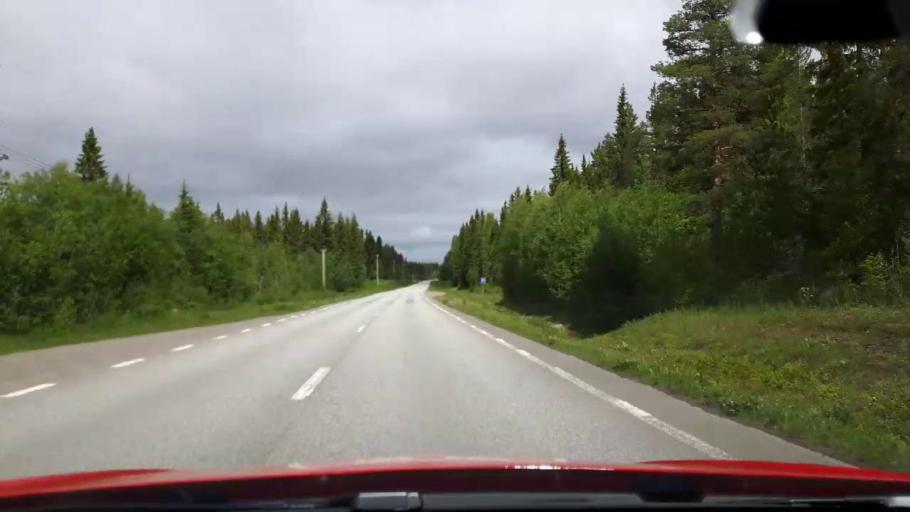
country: SE
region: Jaemtland
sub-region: Krokoms Kommun
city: Krokom
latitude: 63.4861
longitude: 14.5052
